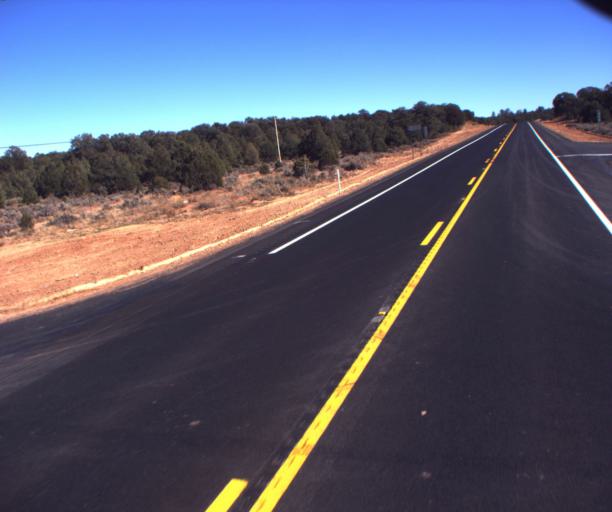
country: US
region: Arizona
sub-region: Apache County
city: Ganado
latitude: 35.7166
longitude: -109.3481
